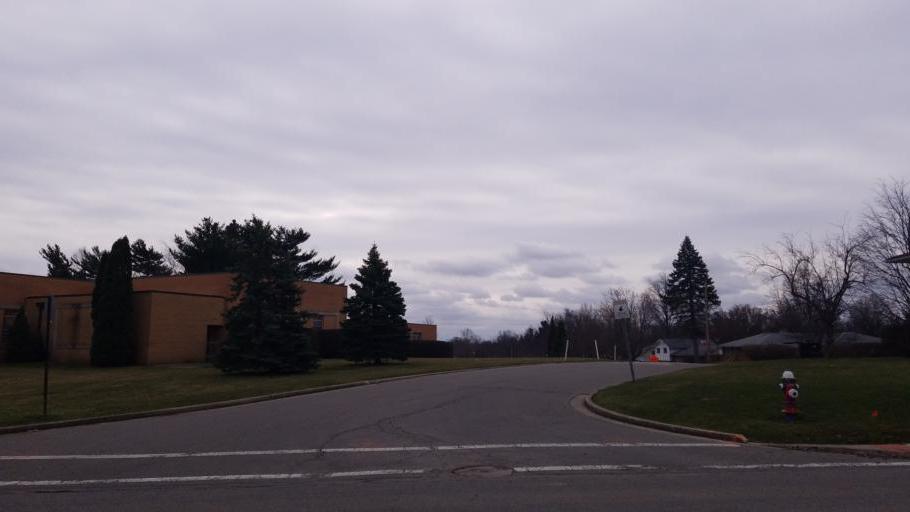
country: US
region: Ohio
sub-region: Richland County
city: Mansfield
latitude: 40.7329
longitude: -82.5287
